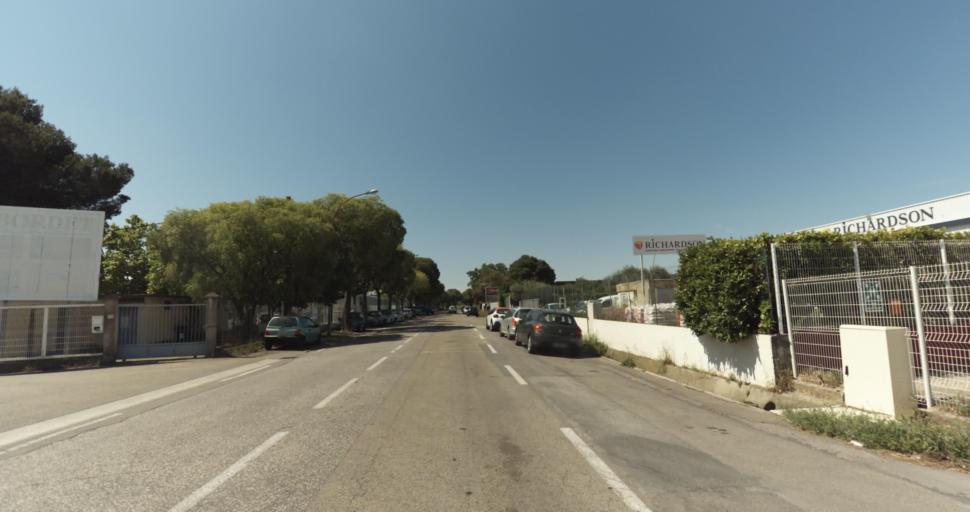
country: FR
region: Languedoc-Roussillon
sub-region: Departement du Gard
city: Milhaud
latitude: 43.8080
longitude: 4.3165
